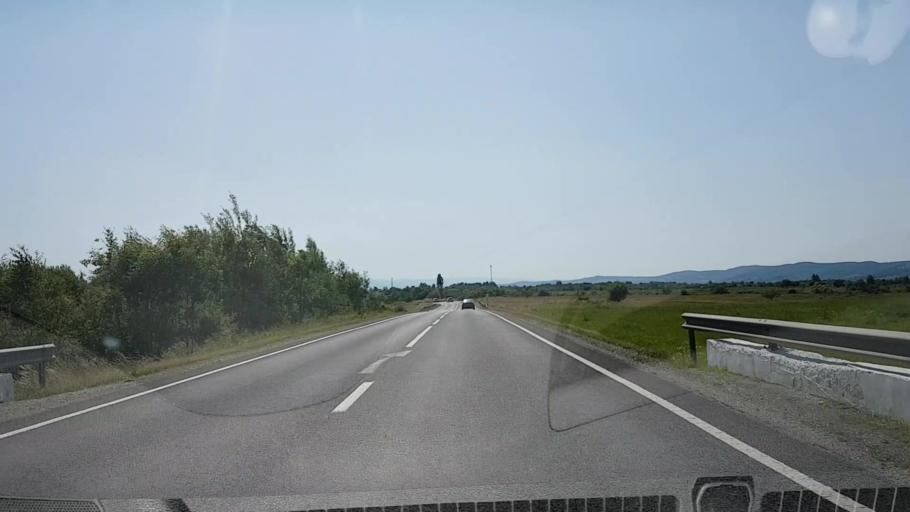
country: RO
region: Sibiu
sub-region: Comuna Carta
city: Carta
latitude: 45.7604
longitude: 24.5604
